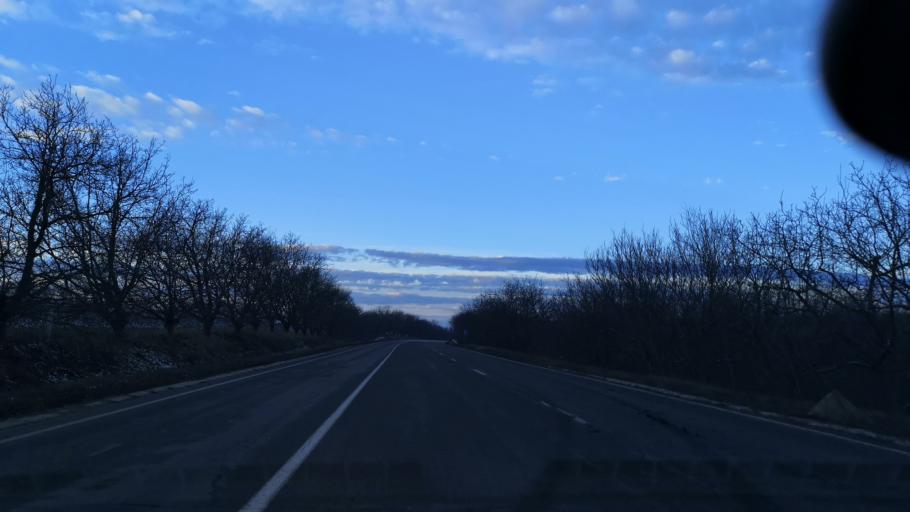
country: MD
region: Orhei
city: Orhei
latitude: 47.5158
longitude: 28.7986
